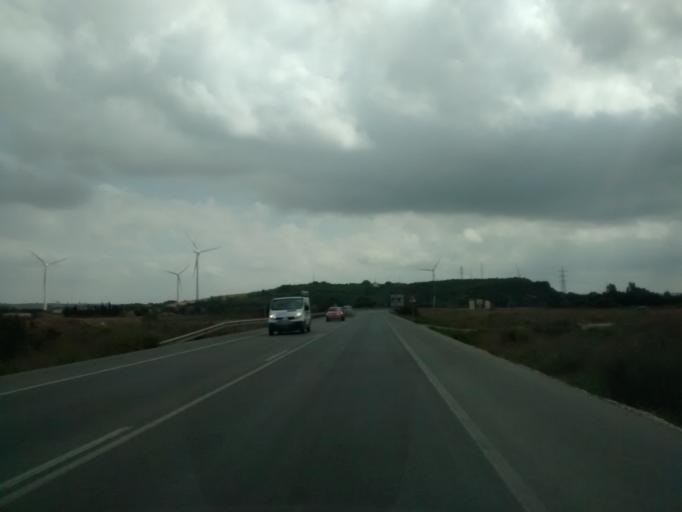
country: ES
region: Andalusia
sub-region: Provincia de Cadiz
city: Chiclana de la Frontera
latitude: 36.4194
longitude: -6.1056
